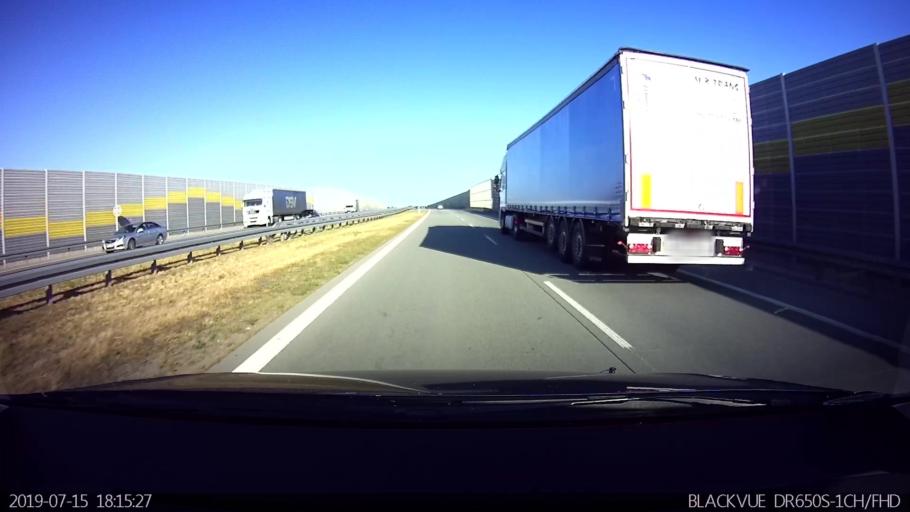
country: PL
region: Lodz Voivodeship
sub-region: Powiat zdunskowolski
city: Zdunska Wola
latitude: 51.5803
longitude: 18.9102
